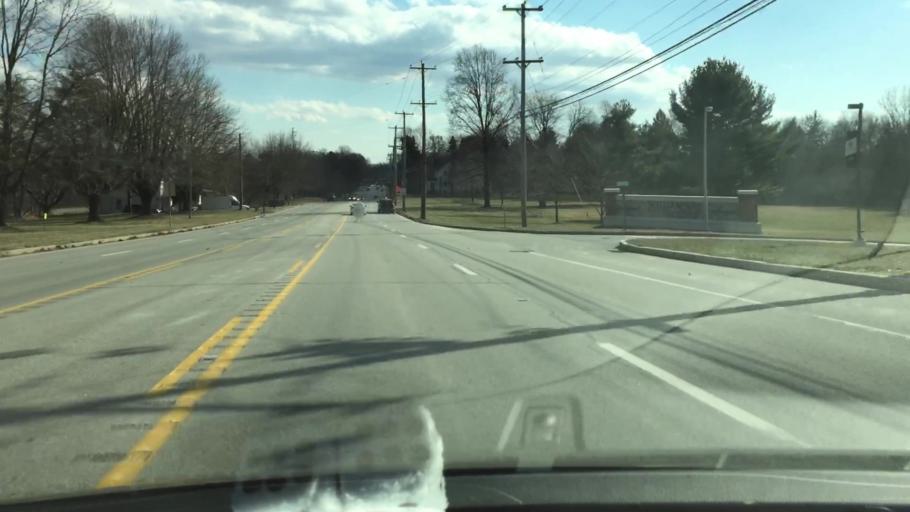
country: US
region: Pennsylvania
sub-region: Delaware County
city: Lima
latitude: 39.9098
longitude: -75.4198
